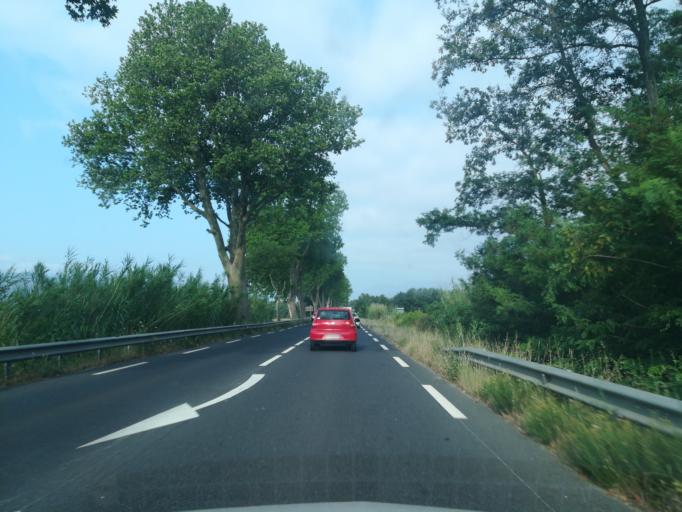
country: FR
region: Languedoc-Roussillon
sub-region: Departement des Pyrenees-Orientales
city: Sant Joan de Pladecorts
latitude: 42.5193
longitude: 2.7992
